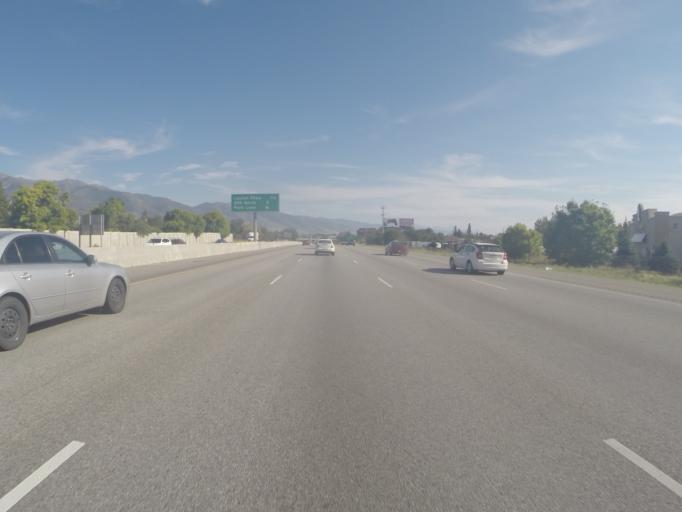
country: US
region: Utah
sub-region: Davis County
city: Layton
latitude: 41.0676
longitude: -111.9710
